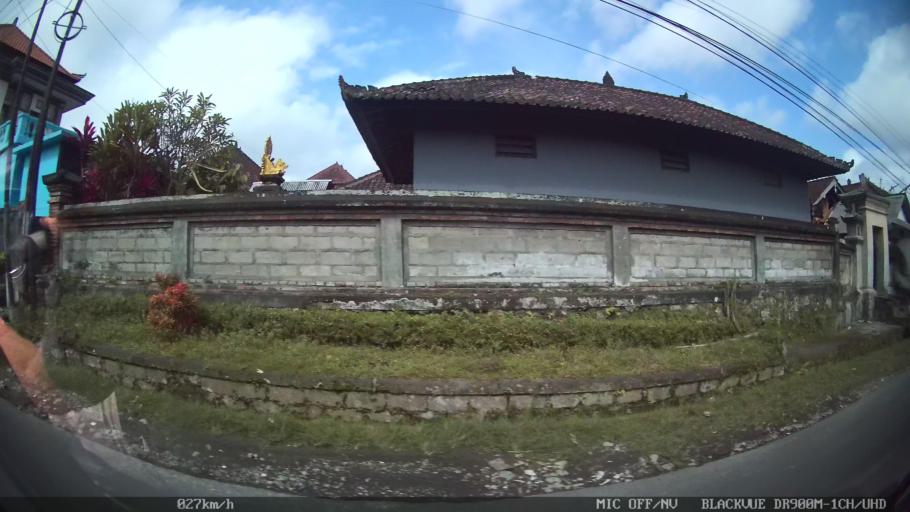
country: ID
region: Bali
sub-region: Kabupaten Gianyar
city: Ubud
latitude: -8.5088
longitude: 115.2824
